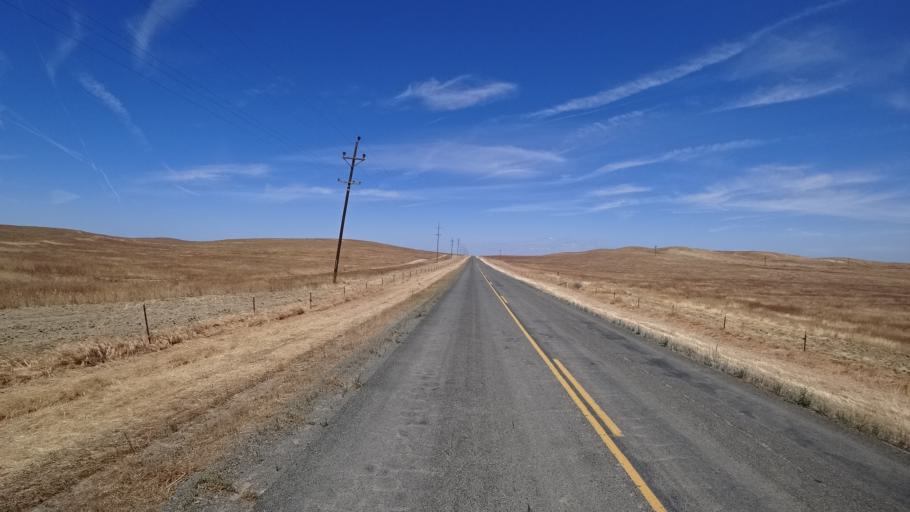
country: US
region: California
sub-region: Kings County
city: Kettleman City
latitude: 35.8590
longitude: -119.9153
